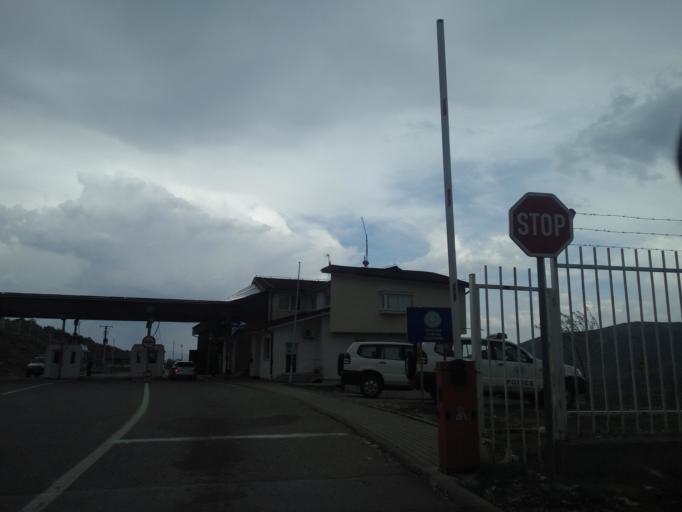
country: XK
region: Gjakova
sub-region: Komuna e Junikut
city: Junik
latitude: 42.4126
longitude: 20.2223
